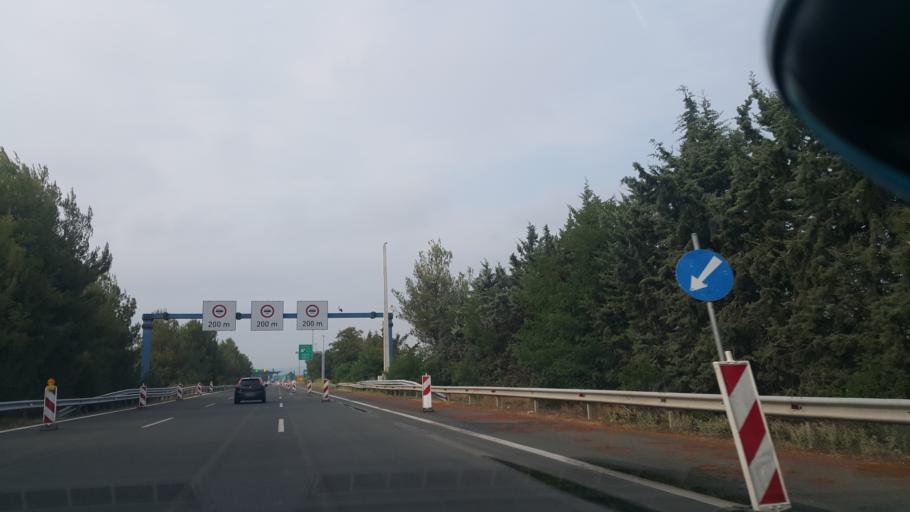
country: GR
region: Central Macedonia
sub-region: Nomos Pierias
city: Aiginio
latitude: 40.5243
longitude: 22.5740
